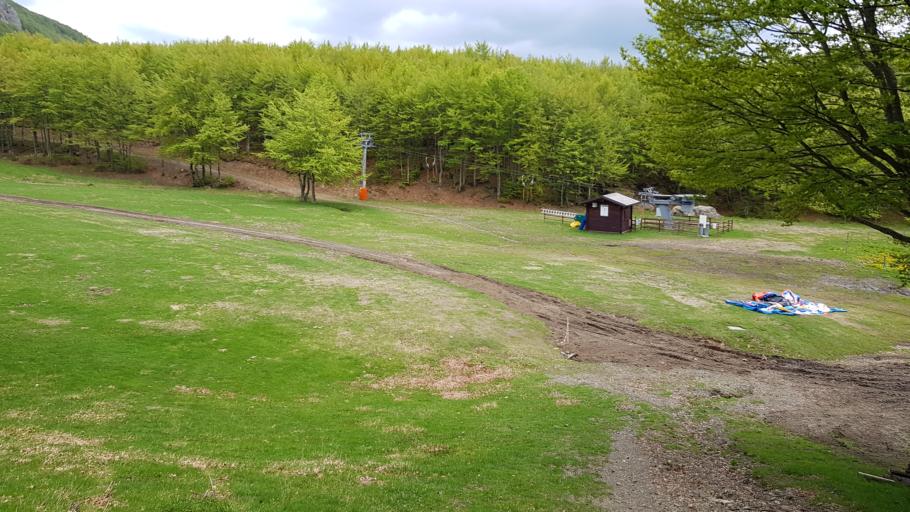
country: IT
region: Liguria
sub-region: Provincia di Genova
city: Santo Stefano d'Aveto
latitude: 44.5587
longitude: 9.4866
